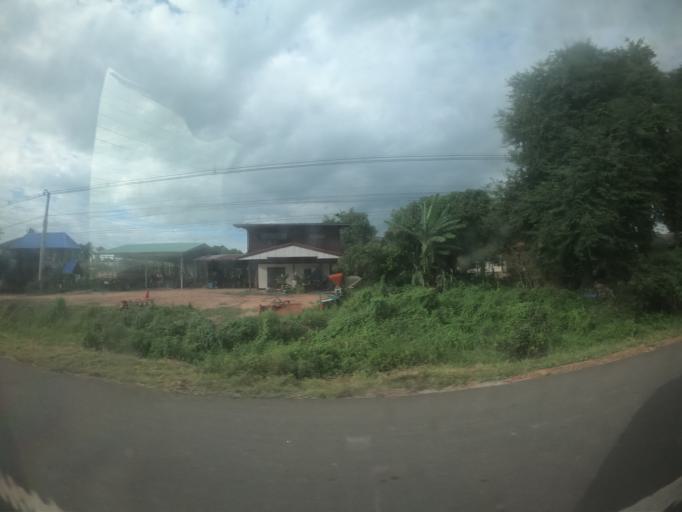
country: TH
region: Surin
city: Kap Choeng
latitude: 14.5304
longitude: 103.5314
